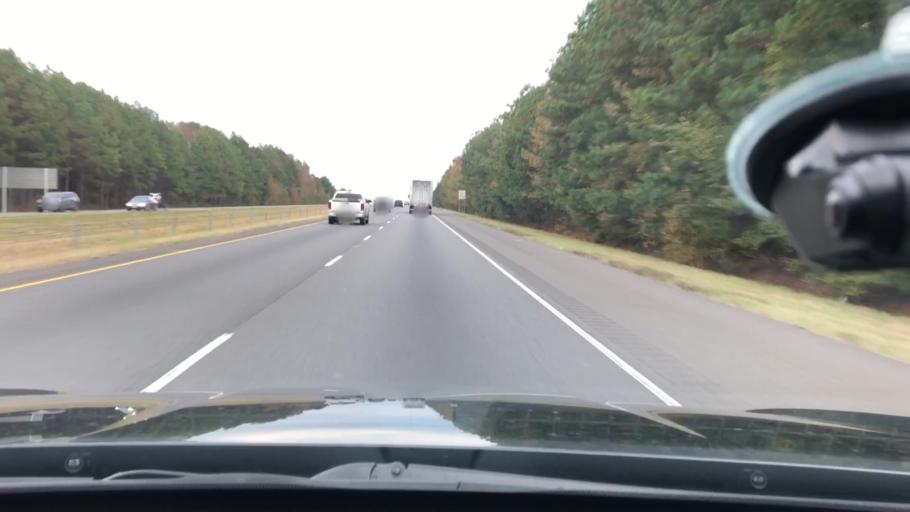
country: US
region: Arkansas
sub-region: Clark County
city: Arkadelphia
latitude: 34.1932
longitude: -93.0598
